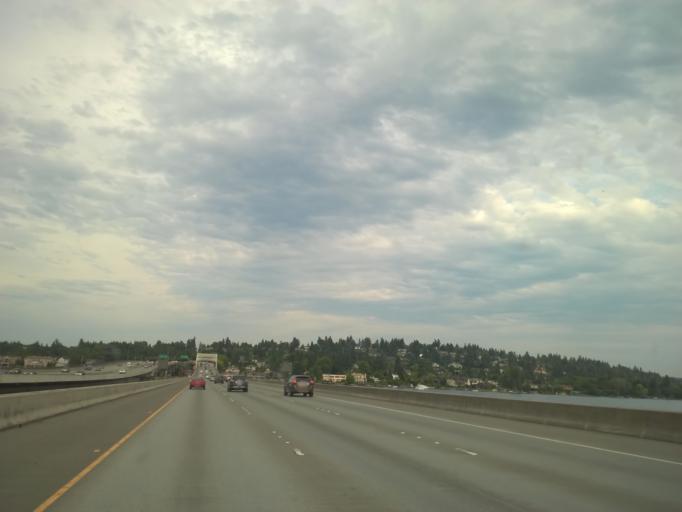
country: US
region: Washington
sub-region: King County
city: Mercer Island
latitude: 47.5893
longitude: -122.2613
